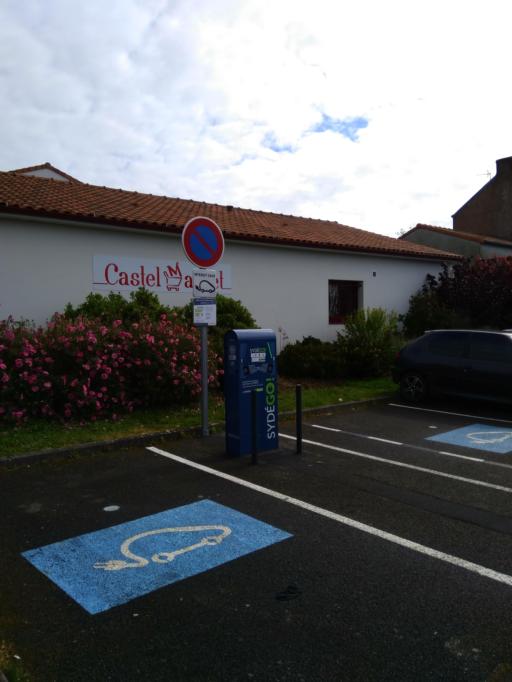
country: FR
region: Pays de la Loire
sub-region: Departement de la Loire-Atlantique
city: Saint-Fiacre-sur-Maine
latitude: 47.1242
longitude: -1.4226
